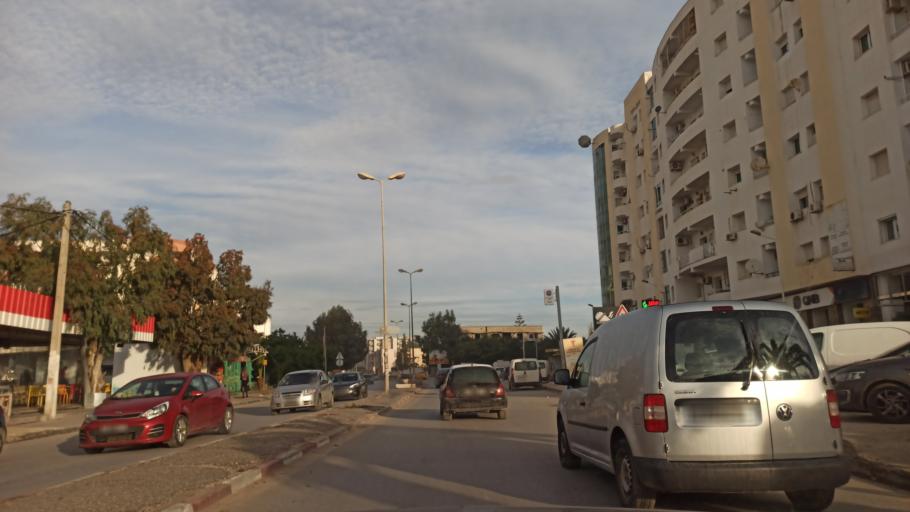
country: TN
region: Ariana
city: Ariana
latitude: 36.8588
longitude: 10.2561
